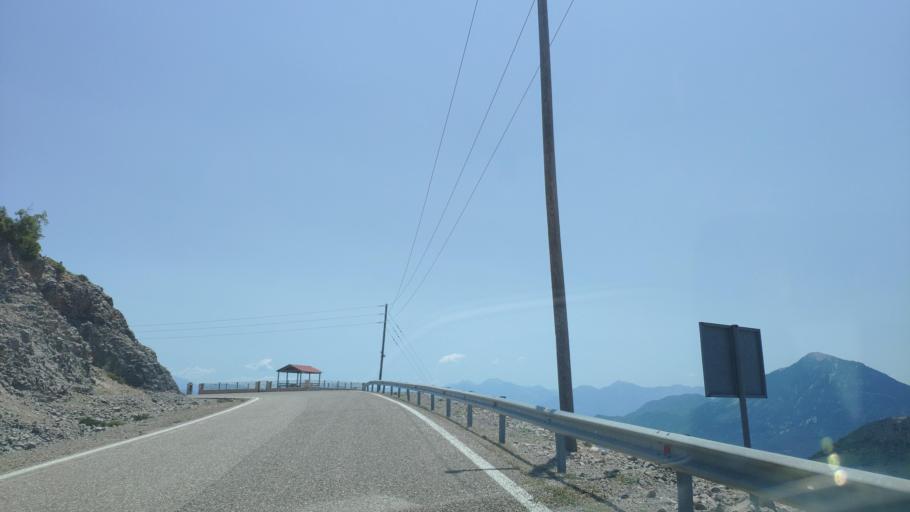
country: GR
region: West Greece
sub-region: Nomos Aitolias kai Akarnanias
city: Krikellos
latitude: 39.0487
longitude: 21.3760
